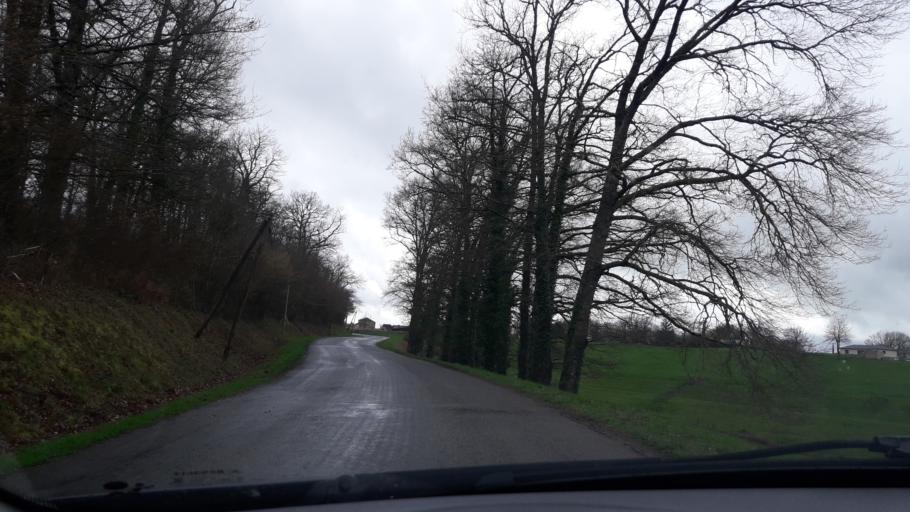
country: FR
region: Limousin
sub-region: Departement de la Haute-Vienne
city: Pierre-Buffiere
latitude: 45.7243
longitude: 1.3788
